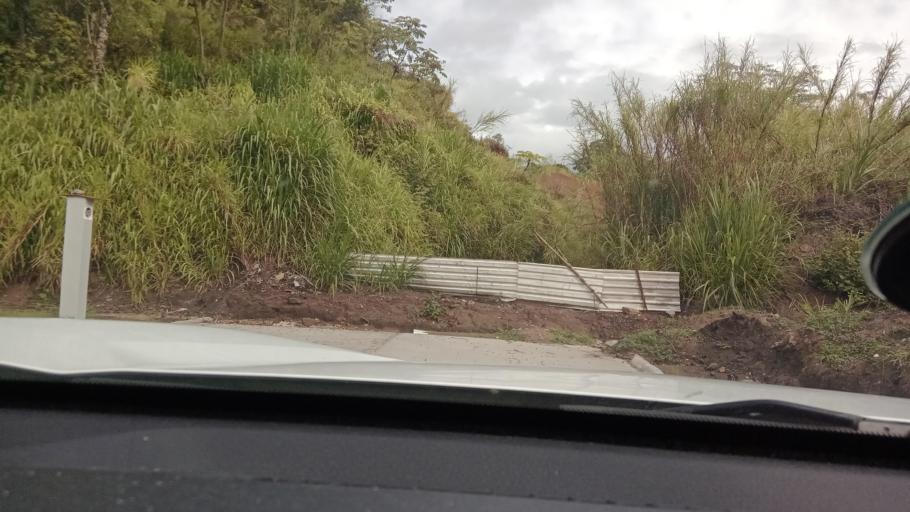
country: MX
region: Veracruz
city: Coatepec
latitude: 19.4401
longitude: -96.9619
